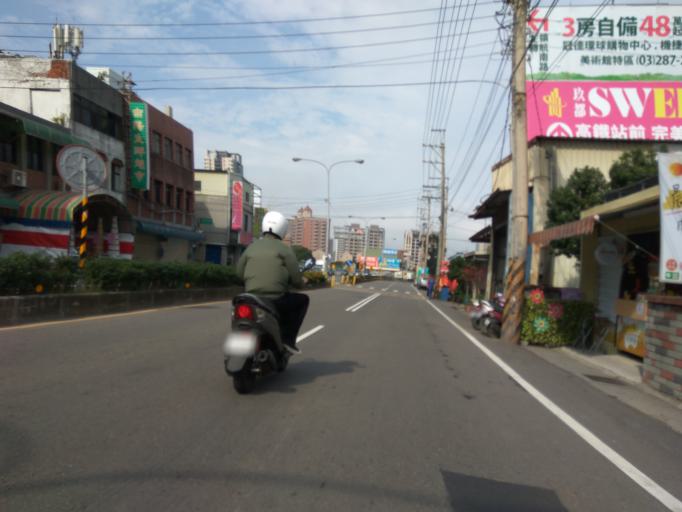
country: TW
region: Taiwan
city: Taoyuan City
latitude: 25.0022
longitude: 121.2154
